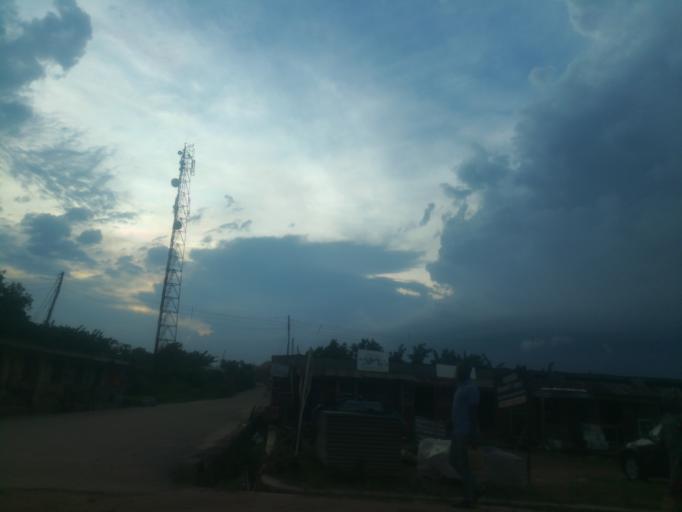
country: NG
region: Oyo
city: Ibadan
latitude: 7.3906
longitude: 3.8364
